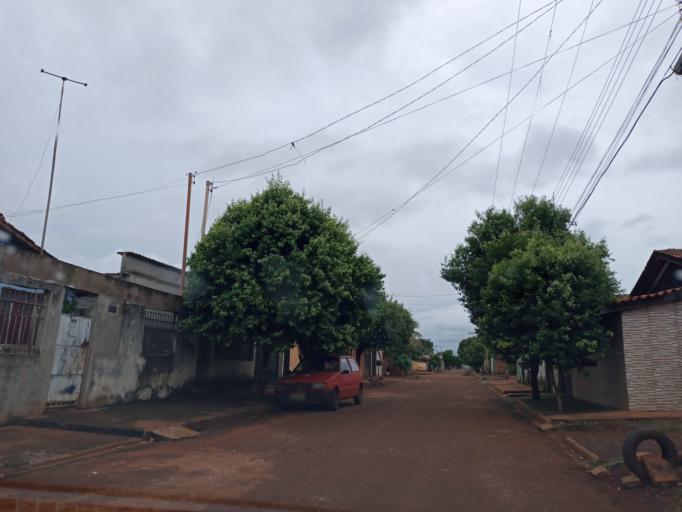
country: BR
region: Minas Gerais
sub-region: Centralina
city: Centralina
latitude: -18.5835
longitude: -49.2080
